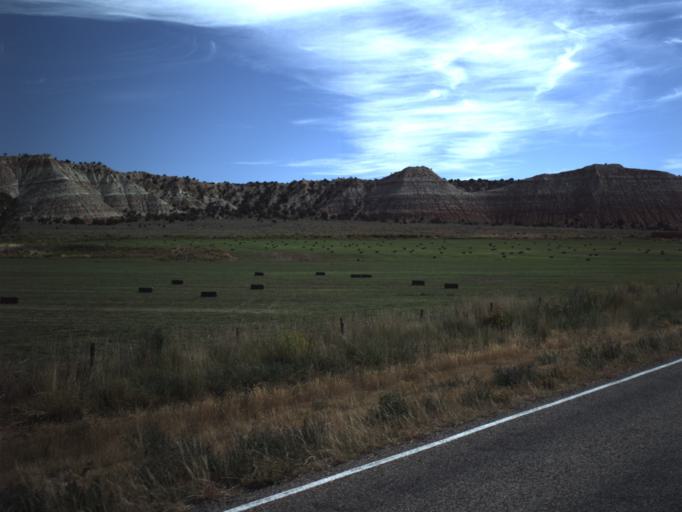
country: US
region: Utah
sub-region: Garfield County
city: Panguitch
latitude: 37.5671
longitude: -112.0504
